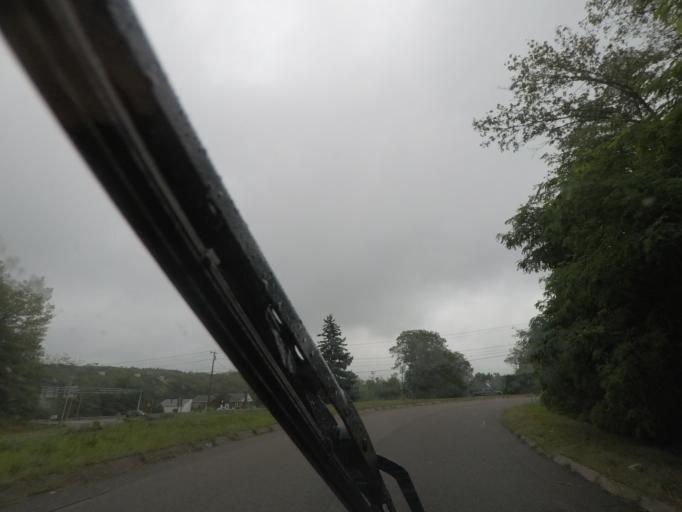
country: US
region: Massachusetts
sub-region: Worcester County
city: Auburn
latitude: 42.1855
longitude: -71.8451
